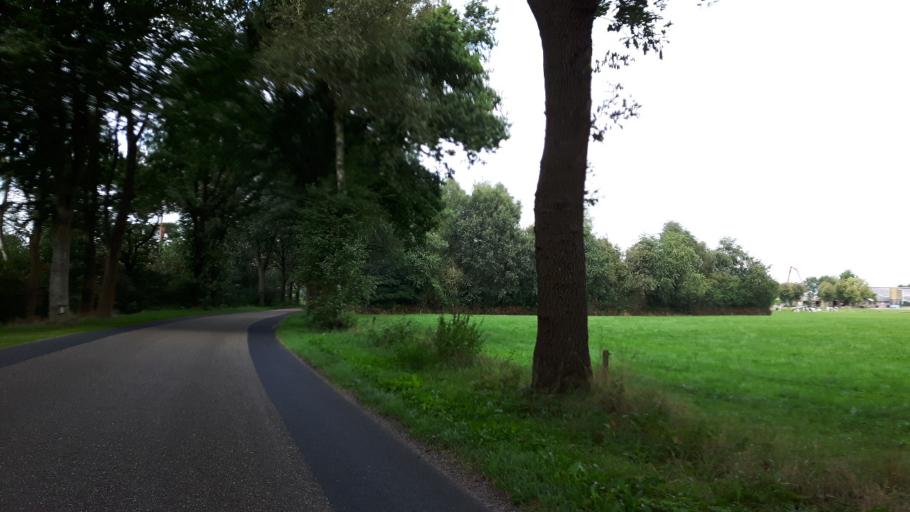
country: NL
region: Groningen
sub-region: Gemeente Leek
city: Leek
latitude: 53.0848
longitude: 6.3205
